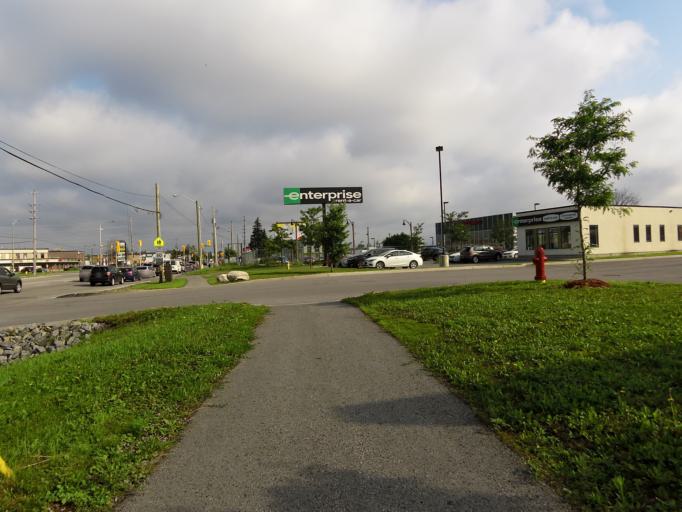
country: CA
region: Ontario
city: Ottawa
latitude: 45.3249
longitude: -75.7182
